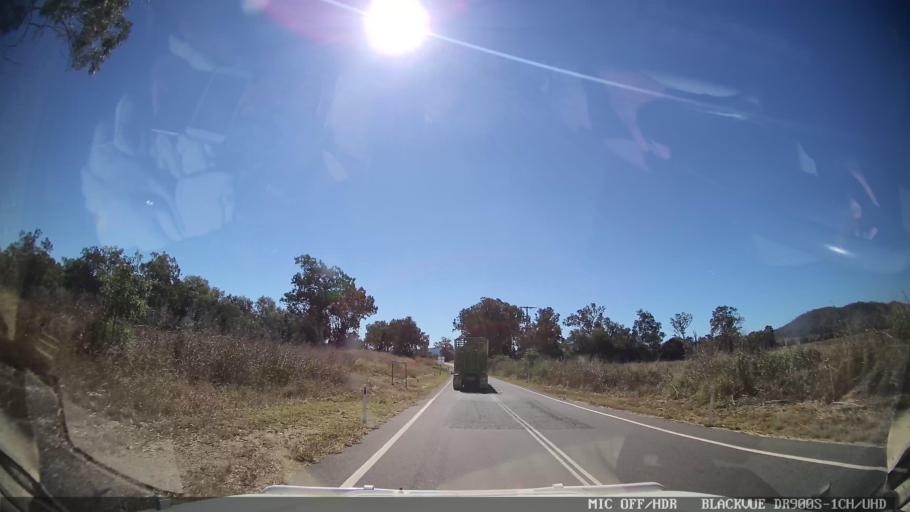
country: AU
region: Queensland
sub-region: Gladstone
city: Toolooa
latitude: -24.2754
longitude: 151.2761
